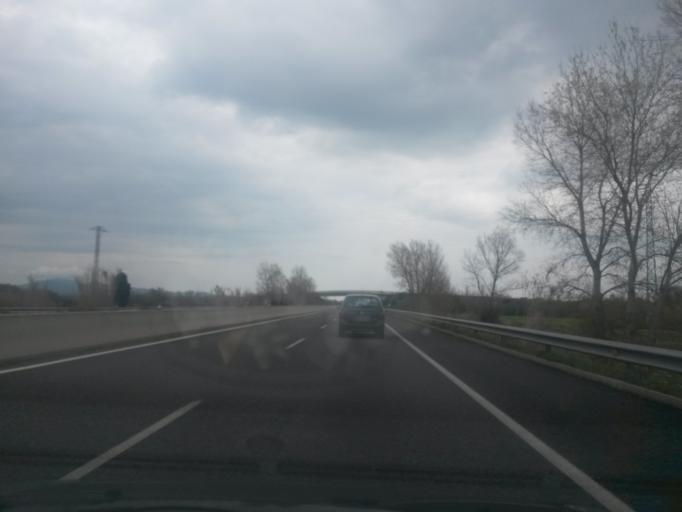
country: ES
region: Catalonia
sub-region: Provincia de Girona
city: Vila-sacra
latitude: 42.2692
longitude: 3.0216
